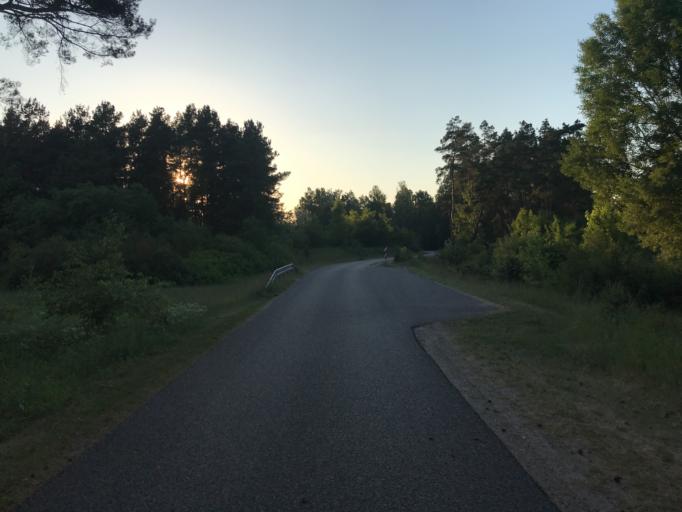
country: DE
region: Brandenburg
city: Melchow
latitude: 52.8326
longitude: 13.6728
